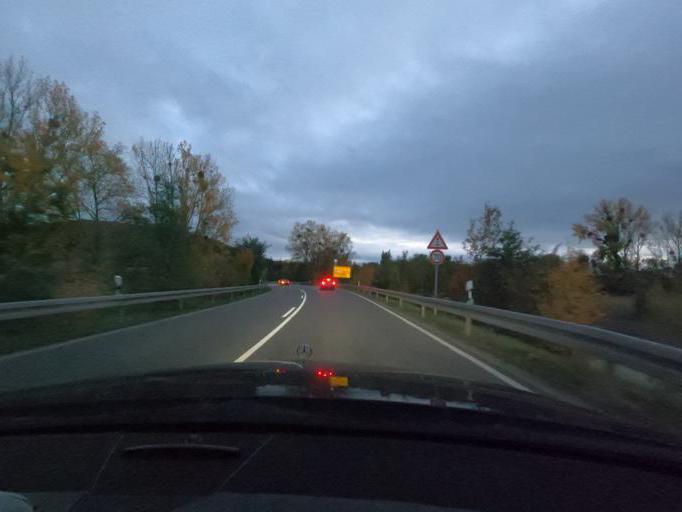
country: DE
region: Thuringia
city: Arenshausen
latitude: 51.3793
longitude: 9.9584
